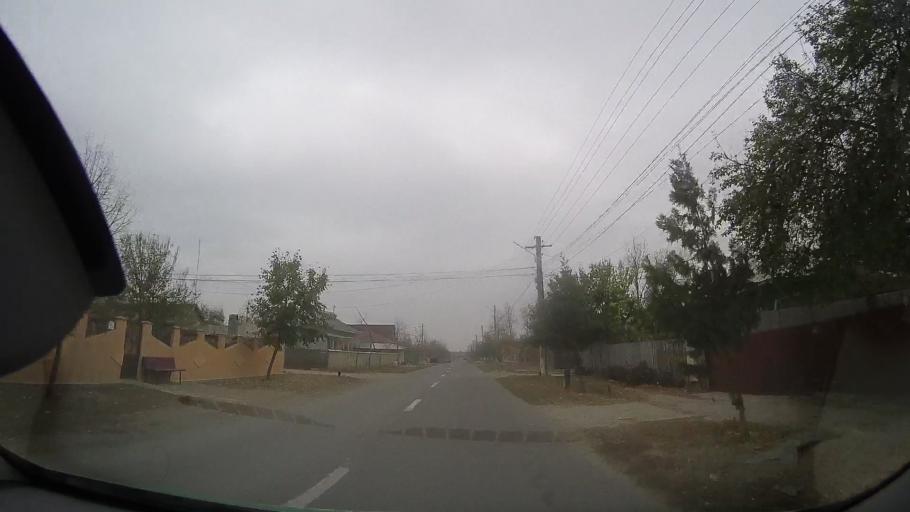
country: RO
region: Ialomita
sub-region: Comuna Grindu
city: Grindu
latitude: 44.7690
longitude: 26.9065
